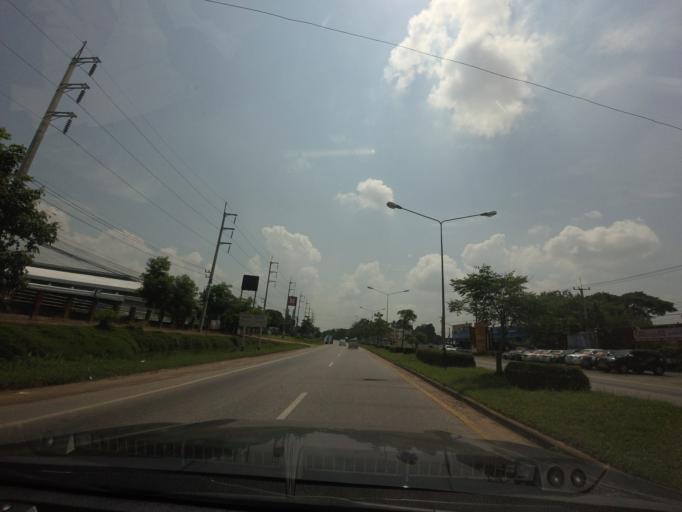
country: TH
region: Uttaradit
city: Uttaradit
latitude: 17.6033
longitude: 100.1240
